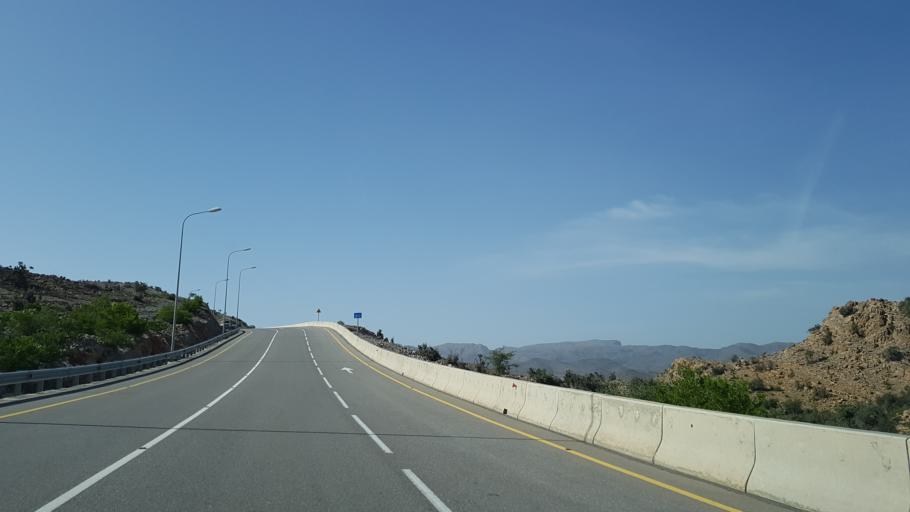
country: OM
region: Muhafazat ad Dakhiliyah
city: Izki
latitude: 23.0427
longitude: 57.7122
